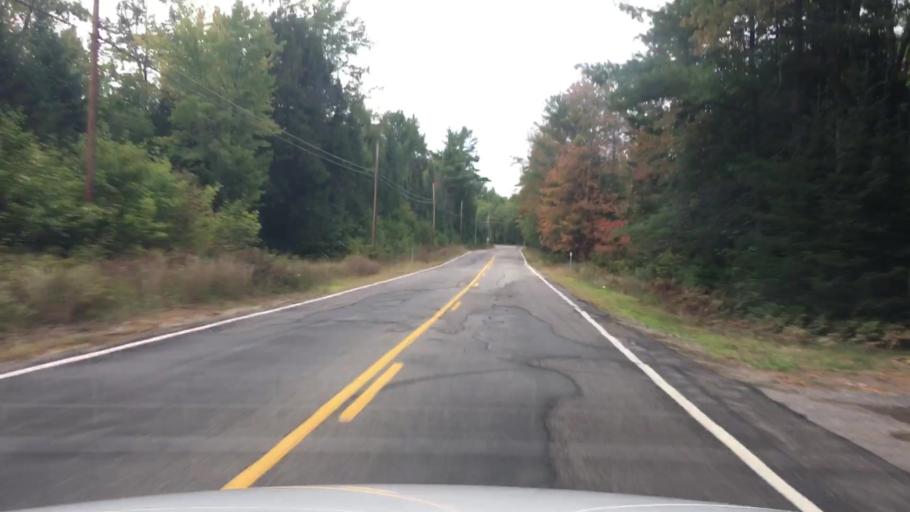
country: US
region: New Hampshire
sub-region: Carroll County
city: Effingham
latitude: 43.7474
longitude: -71.0036
